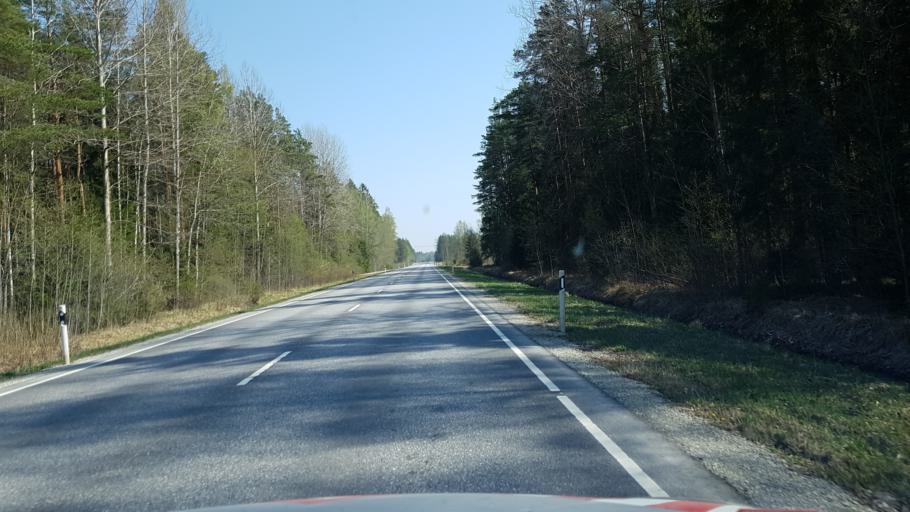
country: EE
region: Paernumaa
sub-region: Vaendra vald (alev)
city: Vandra
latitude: 58.6674
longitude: 25.1684
